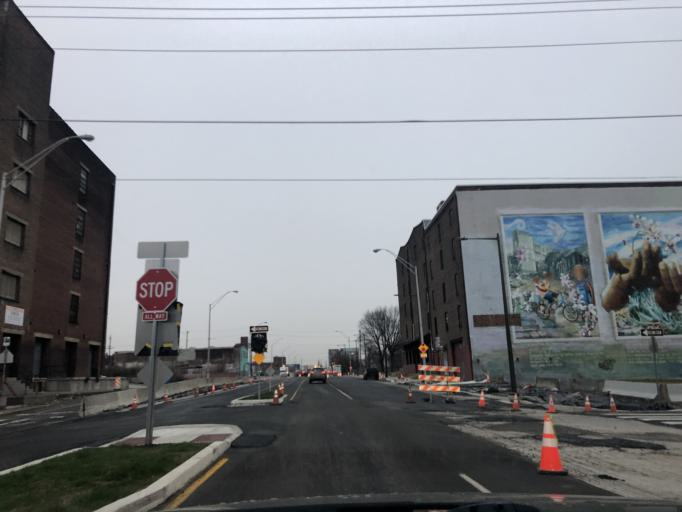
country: US
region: Pennsylvania
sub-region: Philadelphia County
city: Philadelphia
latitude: 39.9868
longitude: -75.1372
